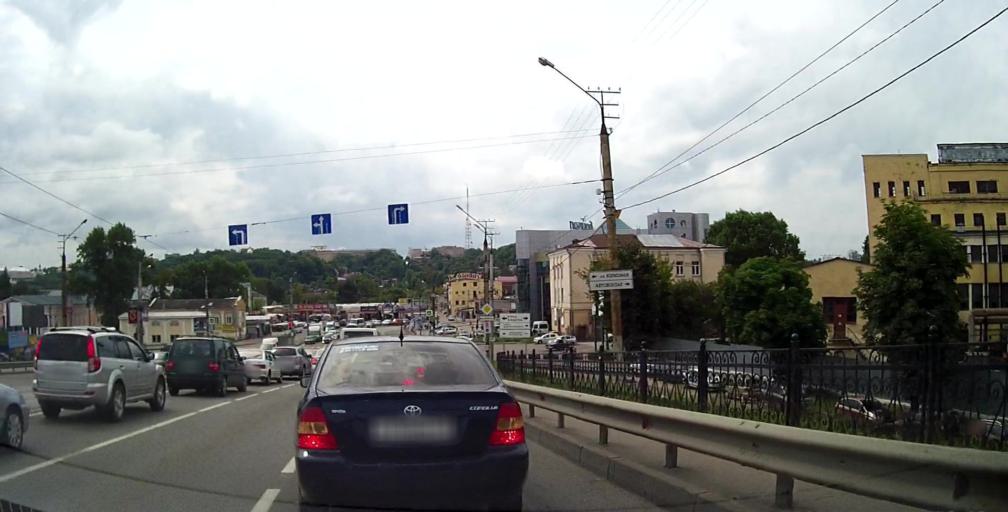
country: RU
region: Smolensk
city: Smolensk
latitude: 54.7962
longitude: 32.0434
